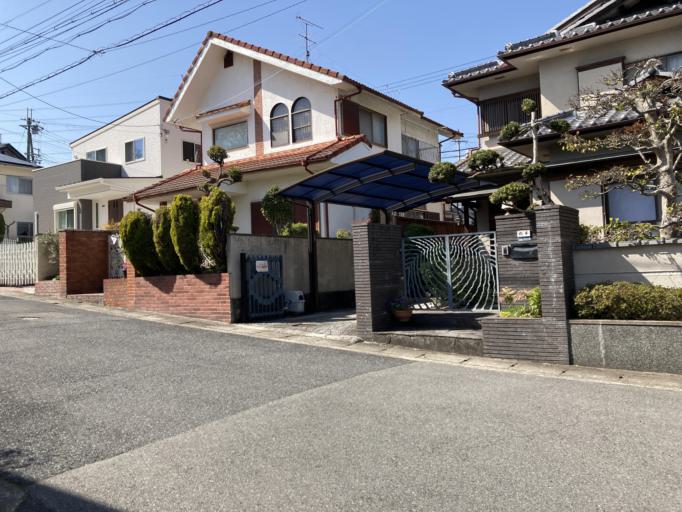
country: JP
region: Nara
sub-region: Ikoma-shi
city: Ikoma
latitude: 34.7091
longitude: 135.6914
